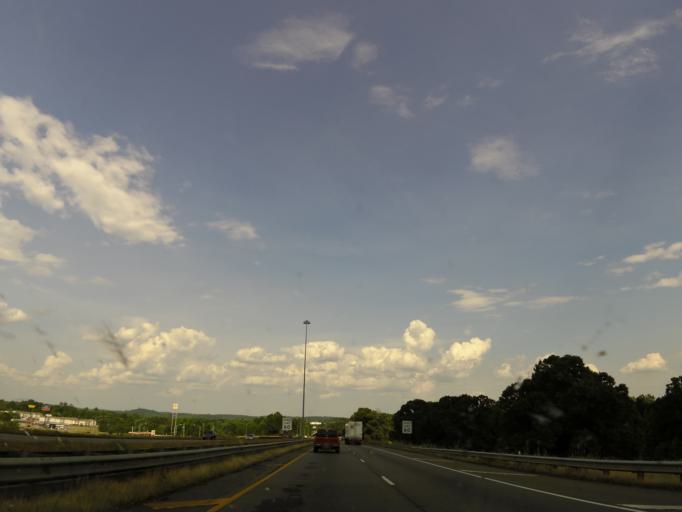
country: US
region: Alabama
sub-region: Tuscaloosa County
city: Holt
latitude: 33.1744
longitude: -87.4768
